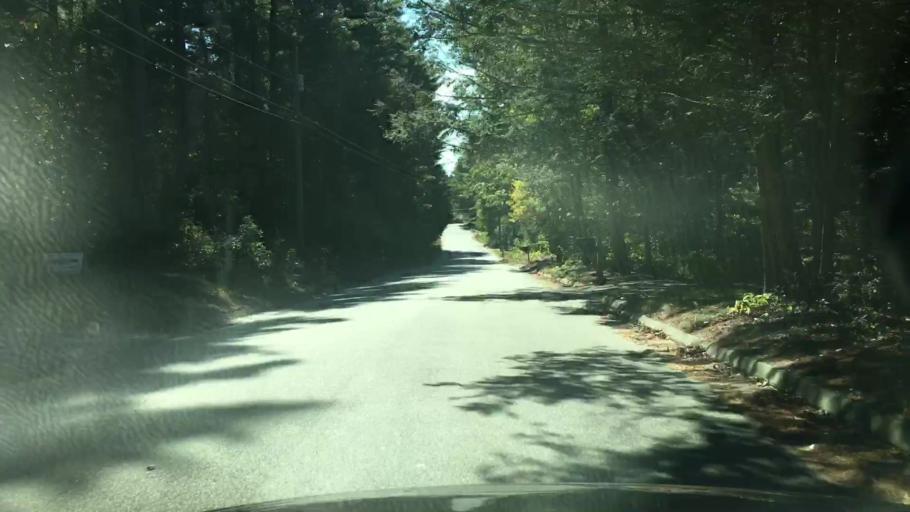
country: US
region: Connecticut
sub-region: Tolland County
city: Stafford Springs
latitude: 41.9808
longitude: -72.3279
